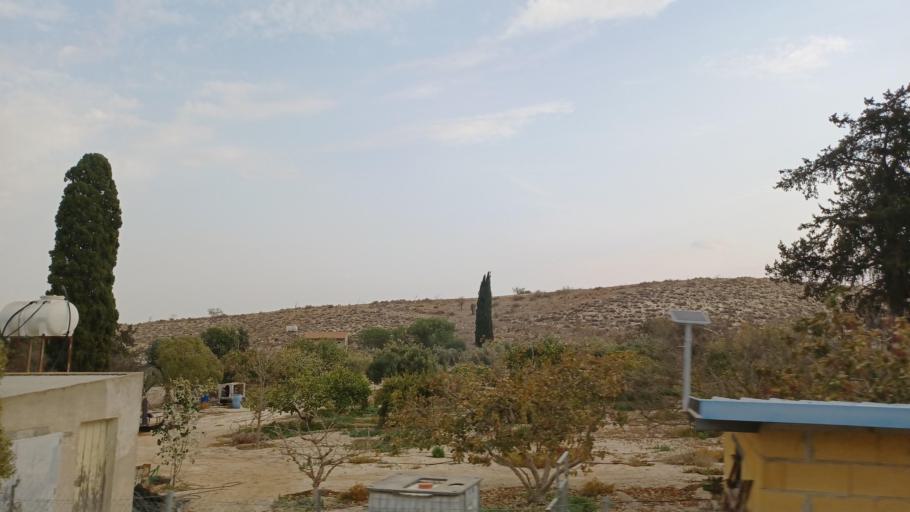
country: CY
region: Larnaka
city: Troulloi
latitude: 35.0310
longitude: 33.5730
